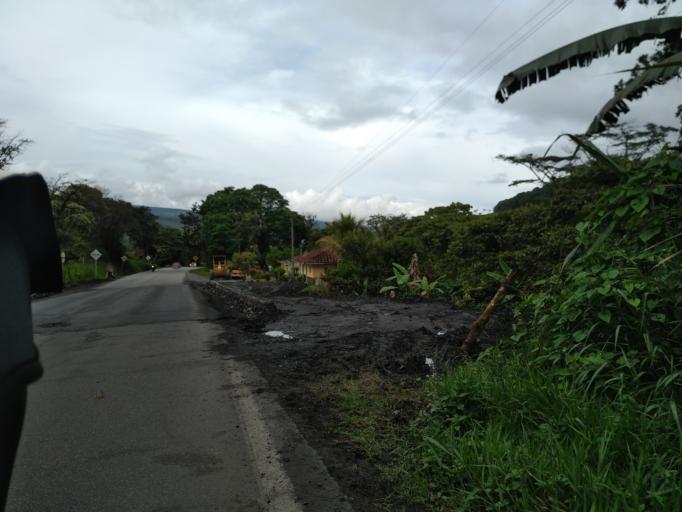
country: CO
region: Santander
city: Suaita
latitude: 6.1327
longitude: -73.3604
